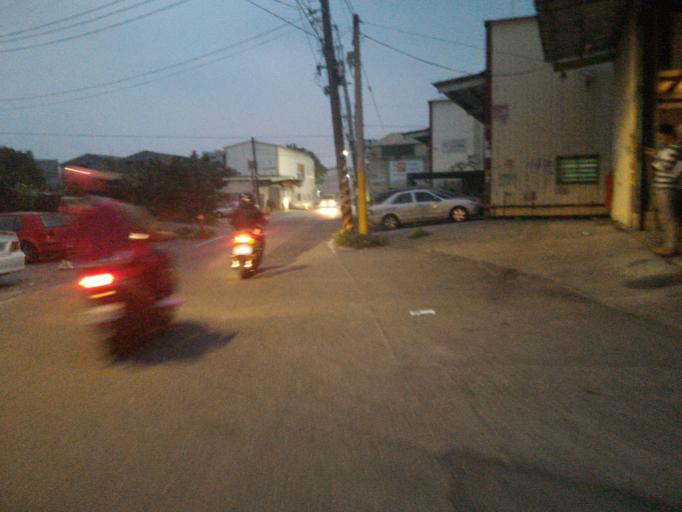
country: TW
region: Taipei
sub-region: Taipei
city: Banqiao
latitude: 24.9530
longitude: 121.4044
